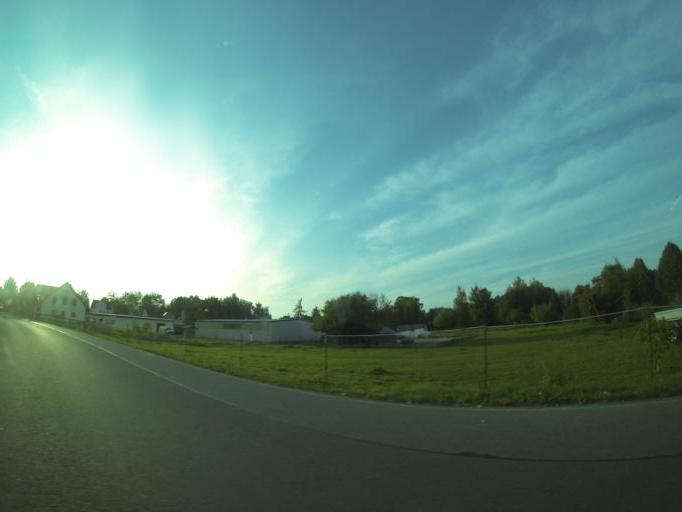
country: DE
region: Thuringia
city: Altkirchen
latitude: 50.9332
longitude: 12.3493
